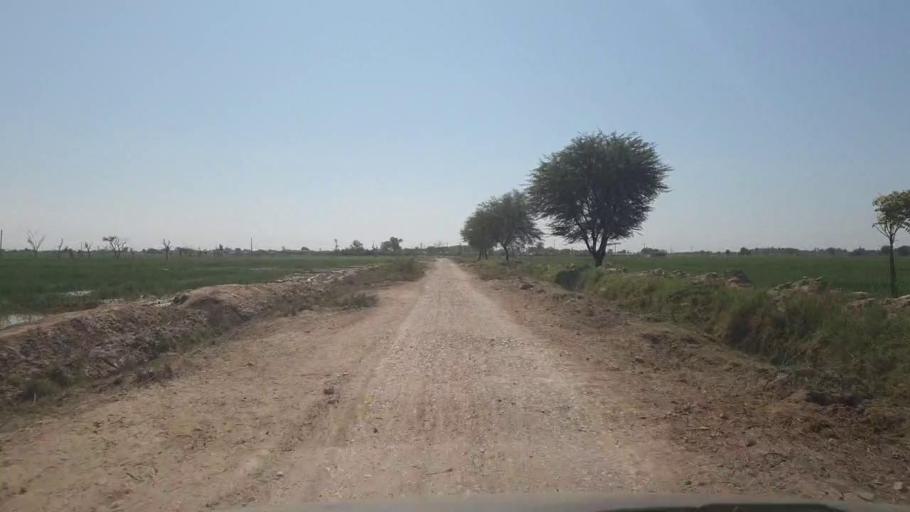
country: PK
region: Sindh
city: Dhoro Naro
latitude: 25.4744
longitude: 69.6135
